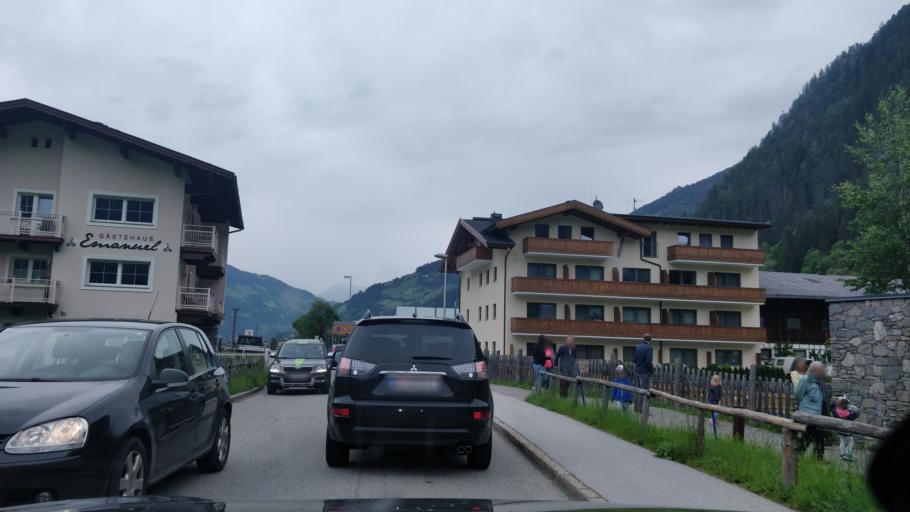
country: AT
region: Tyrol
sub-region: Politischer Bezirk Schwaz
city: Mayrhofen
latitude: 47.1780
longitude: 11.8703
